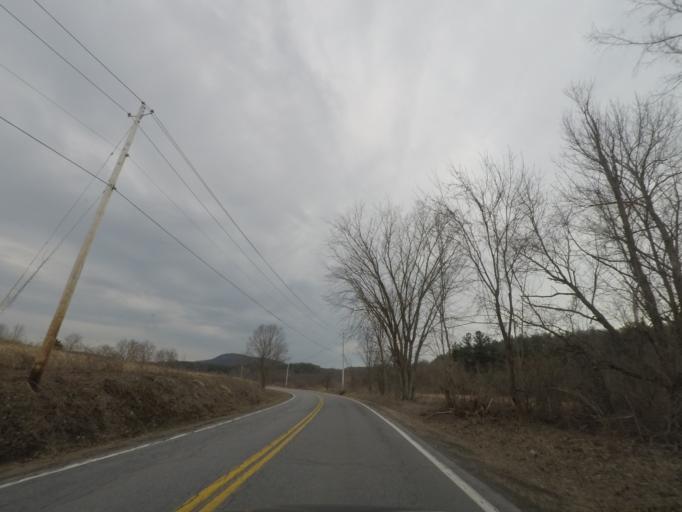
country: US
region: New York
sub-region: Washington County
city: Greenwich
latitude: 43.0603
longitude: -73.5010
